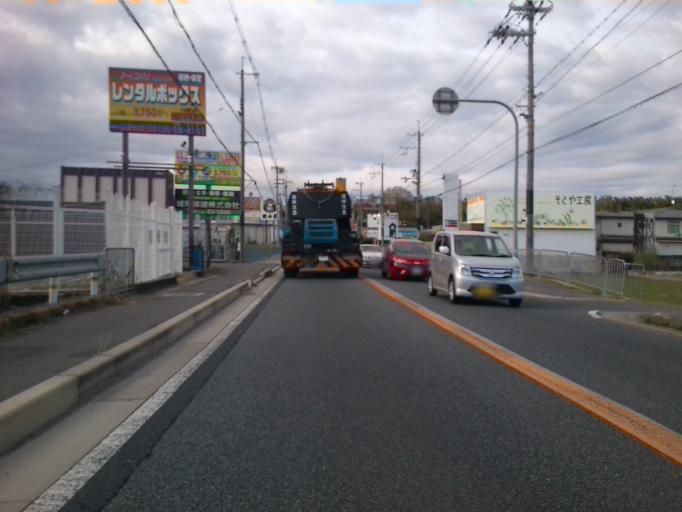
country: JP
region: Kyoto
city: Tanabe
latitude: 34.8307
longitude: 135.7929
